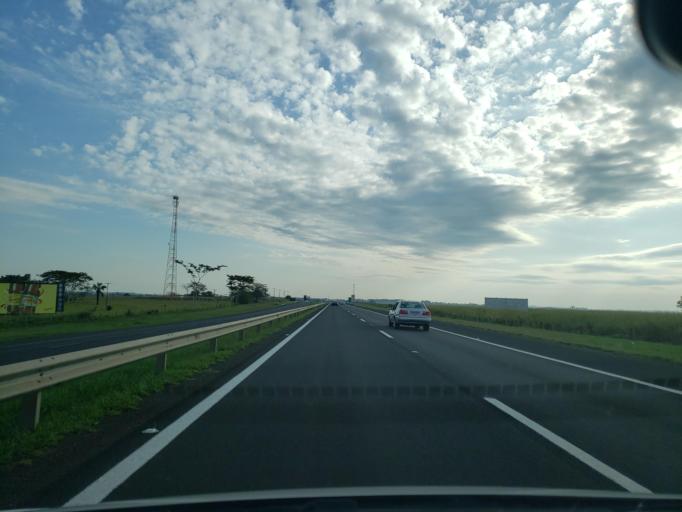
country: BR
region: Sao Paulo
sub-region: Guararapes
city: Guararapes
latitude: -21.2057
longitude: -50.6317
